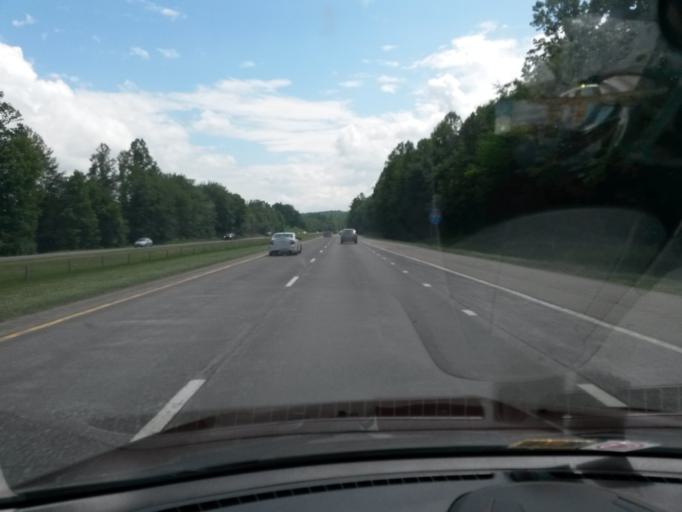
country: US
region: North Carolina
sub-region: Surry County
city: Dobson
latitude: 36.4760
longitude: -80.7538
